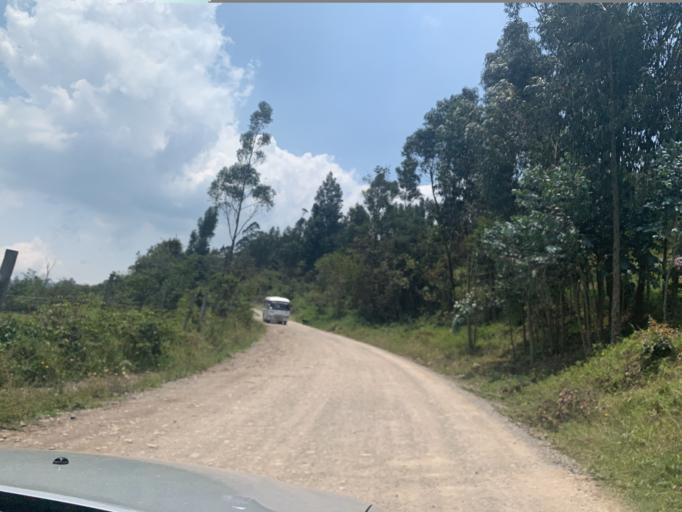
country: CO
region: Boyaca
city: Chiquinquira
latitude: 5.5890
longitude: -73.7496
